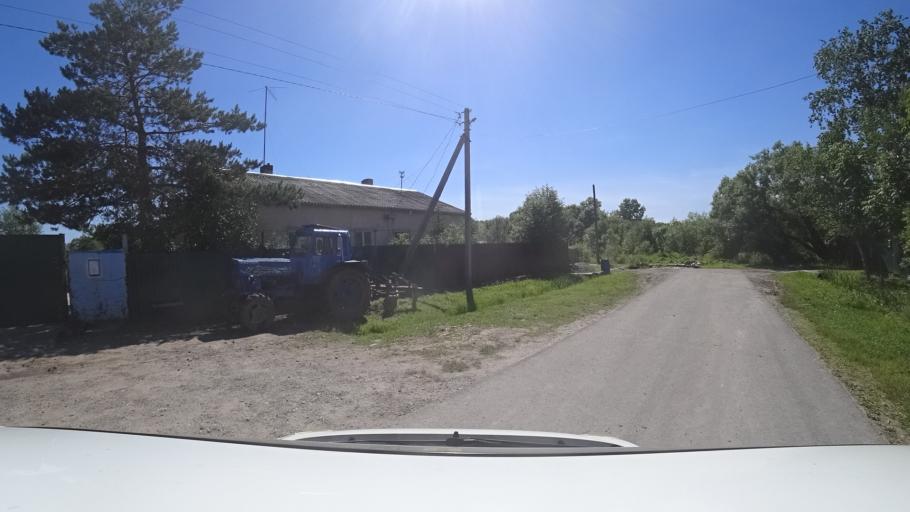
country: RU
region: Khabarovsk Krai
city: Topolevo
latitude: 48.5571
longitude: 135.1868
